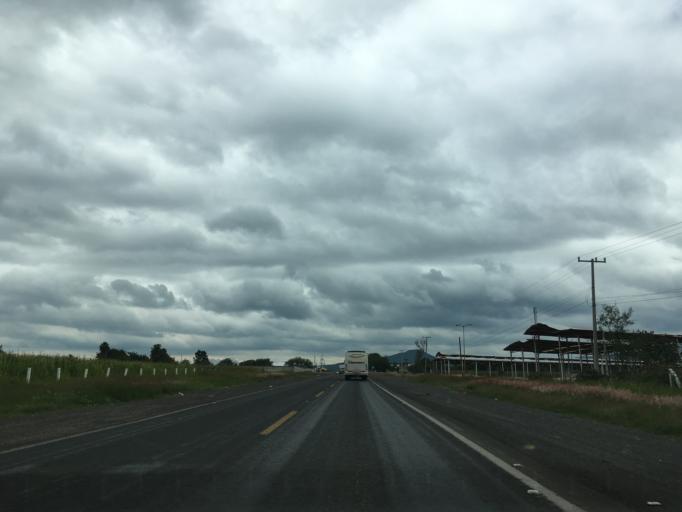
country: MX
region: Michoacan
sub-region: Cuitzeo
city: Cuamio
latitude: 20.0521
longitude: -101.1505
